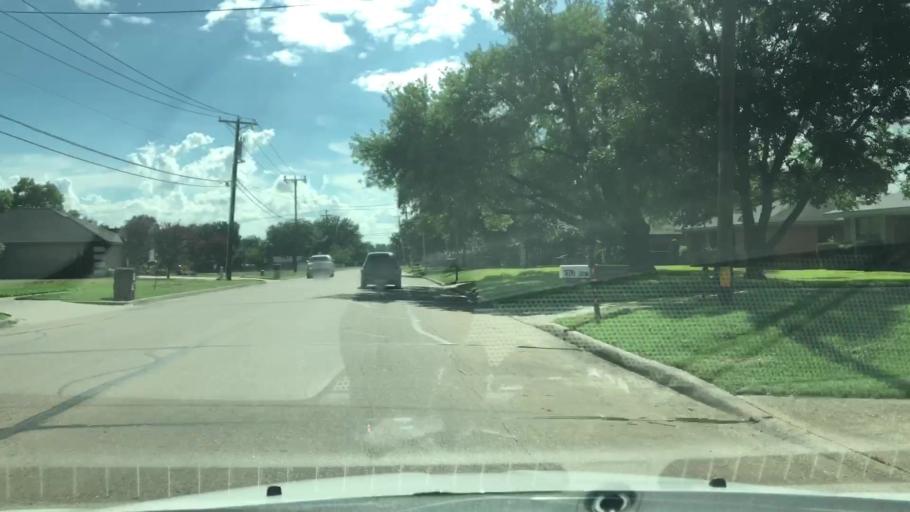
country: US
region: Texas
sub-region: Ellis County
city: Ennis
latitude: 32.3499
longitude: -96.6455
